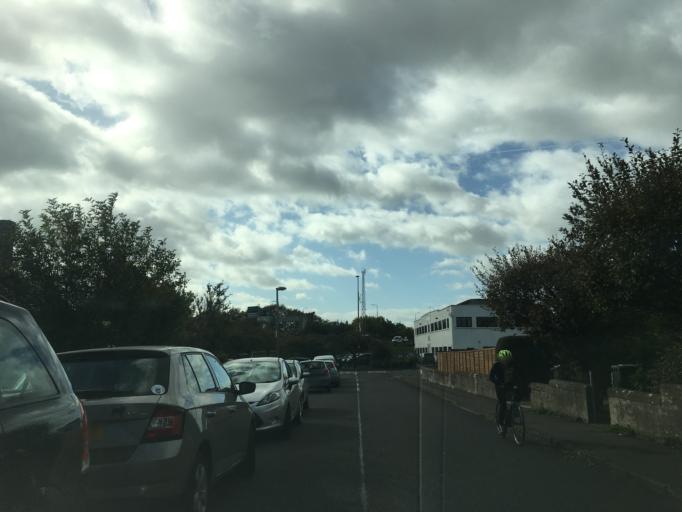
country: GB
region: Scotland
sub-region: Edinburgh
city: Currie
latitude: 55.9415
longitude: -3.3147
